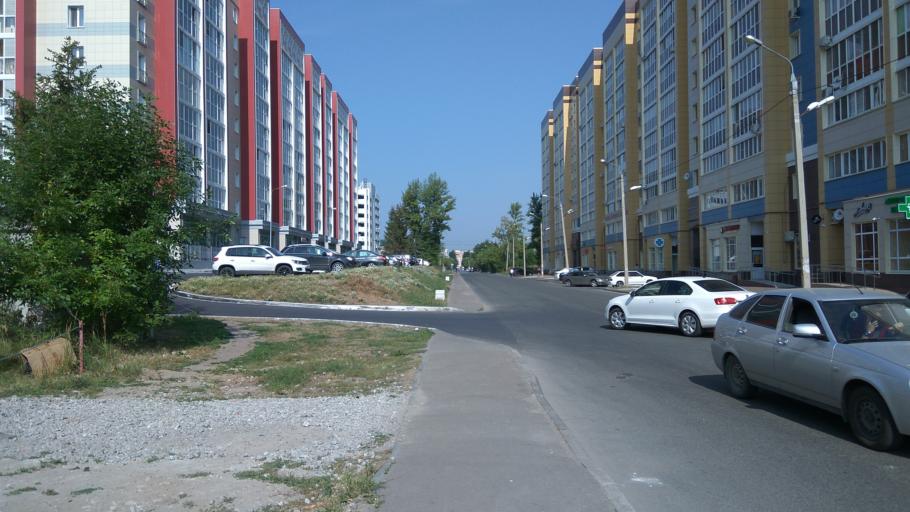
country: RU
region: Tatarstan
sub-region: Gorod Kazan'
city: Kazan
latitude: 55.7684
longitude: 49.1539
